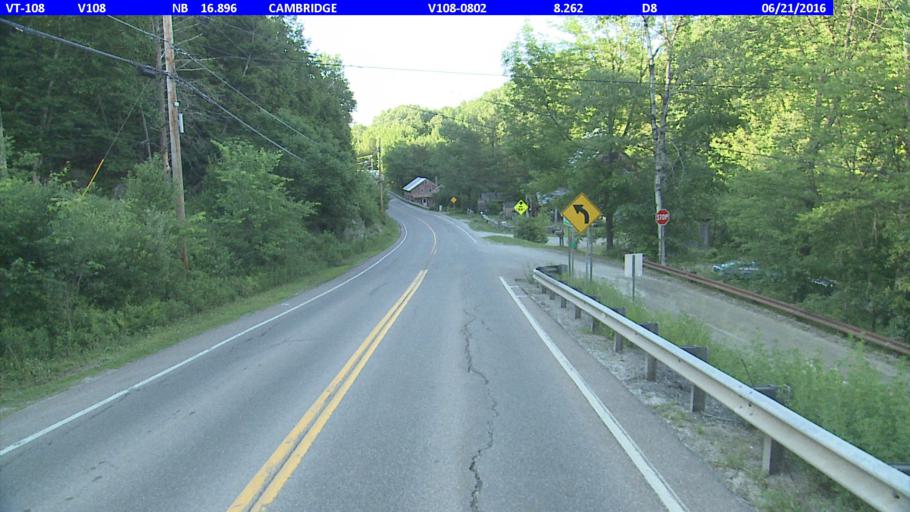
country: US
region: Vermont
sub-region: Lamoille County
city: Johnson
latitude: 44.6373
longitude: -72.8259
